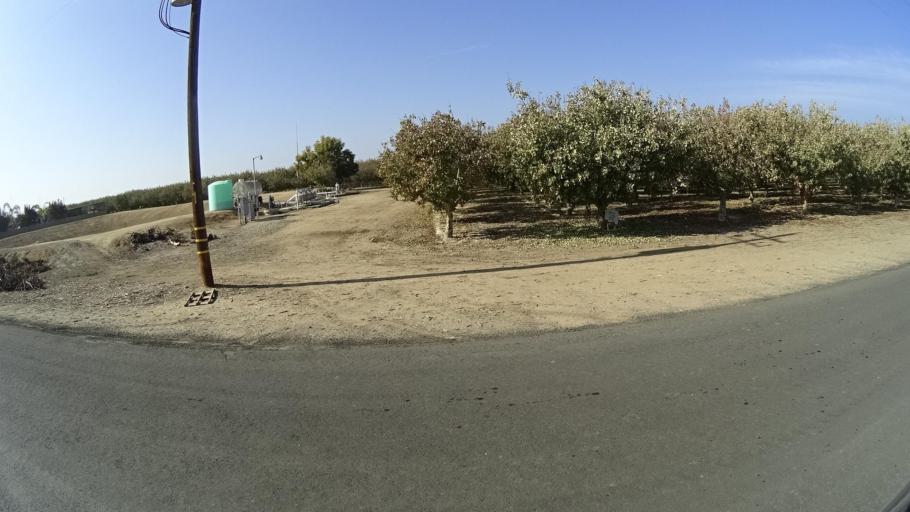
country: US
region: California
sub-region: Kern County
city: McFarland
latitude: 35.6399
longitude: -119.1866
